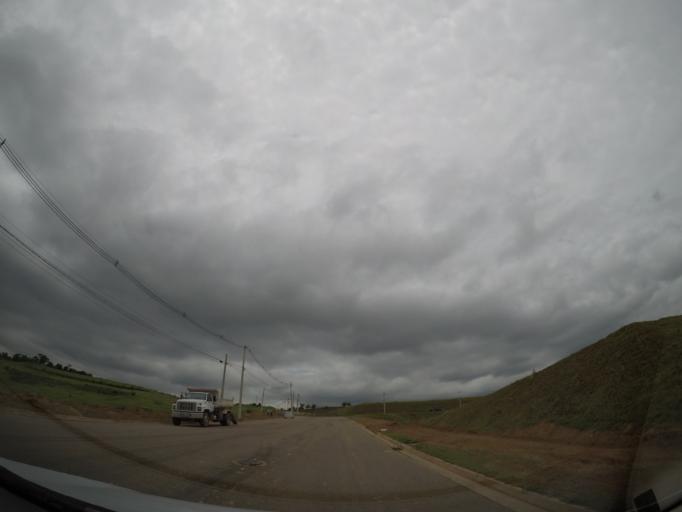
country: BR
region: Sao Paulo
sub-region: Vinhedo
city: Vinhedo
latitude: -23.0751
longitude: -47.0082
